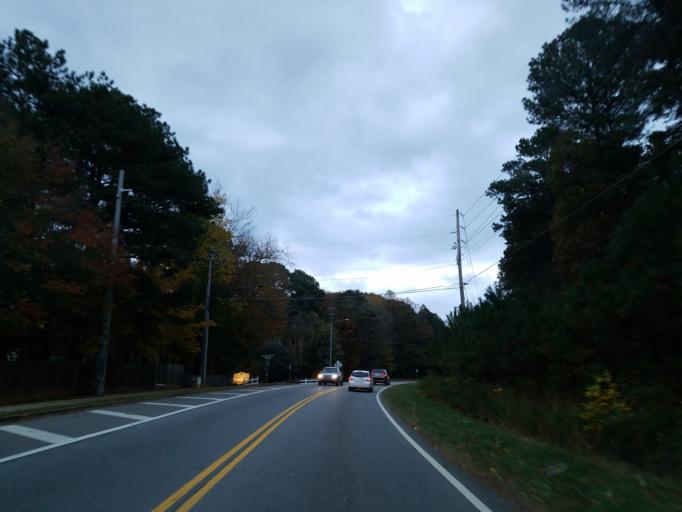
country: US
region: Georgia
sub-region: Cobb County
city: Kennesaw
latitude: 34.0629
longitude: -84.6028
